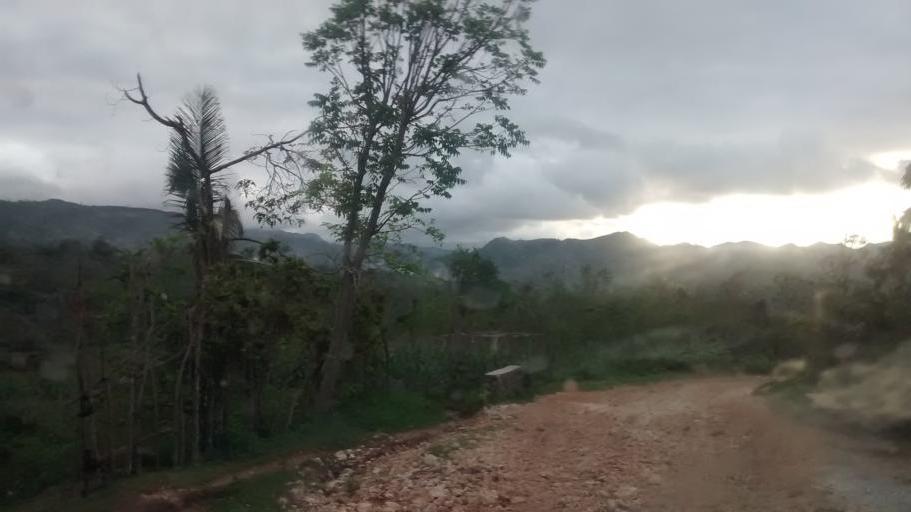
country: HT
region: Grandans
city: Corail
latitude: 18.4765
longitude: -73.7925
